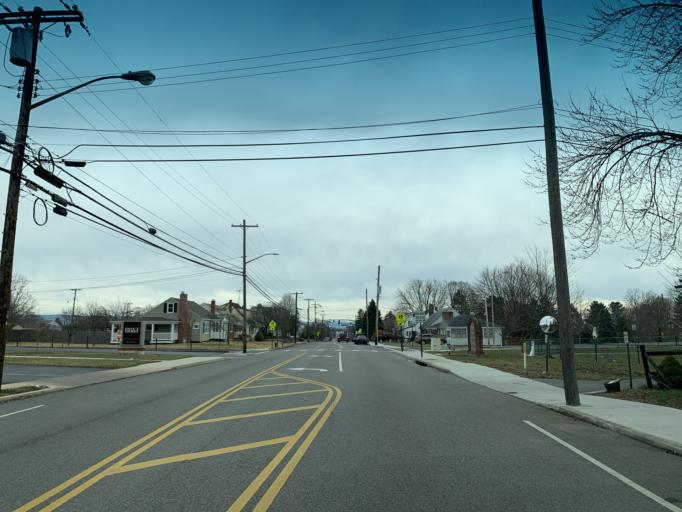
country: US
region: Maryland
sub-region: Washington County
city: Hagerstown
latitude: 39.6581
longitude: -77.7355
